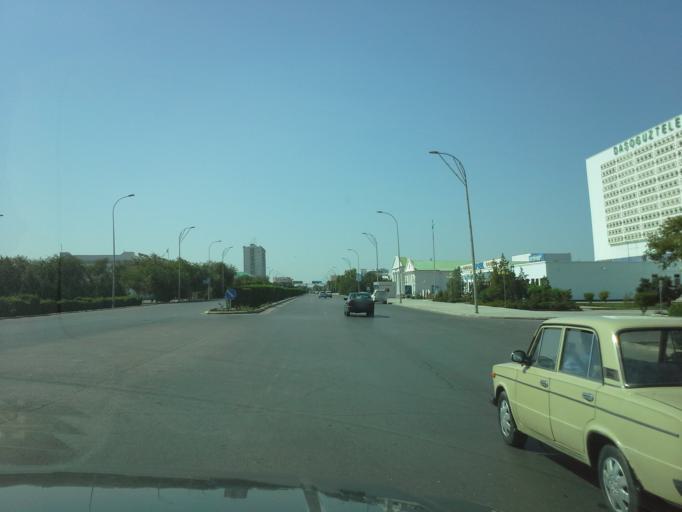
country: TM
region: Dasoguz
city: Dasoguz
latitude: 41.8343
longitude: 59.9664
